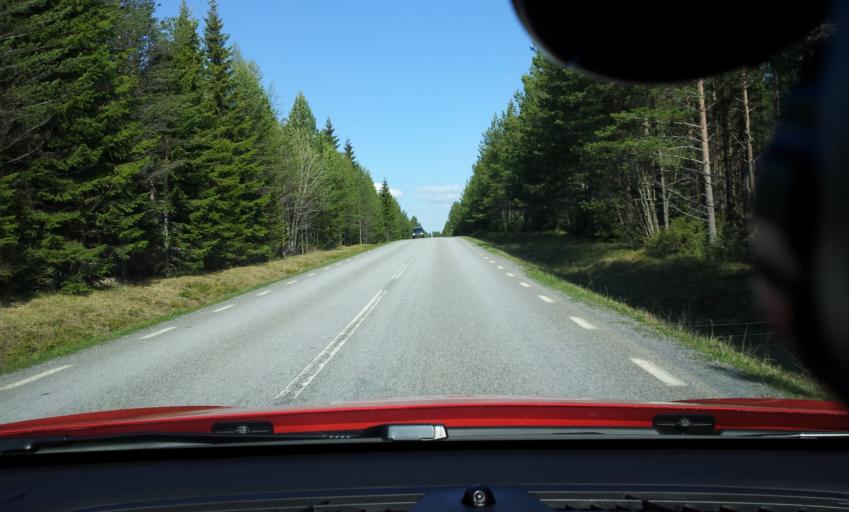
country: SE
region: Jaemtland
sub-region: Krokoms Kommun
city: Krokom
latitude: 63.1305
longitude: 14.2108
